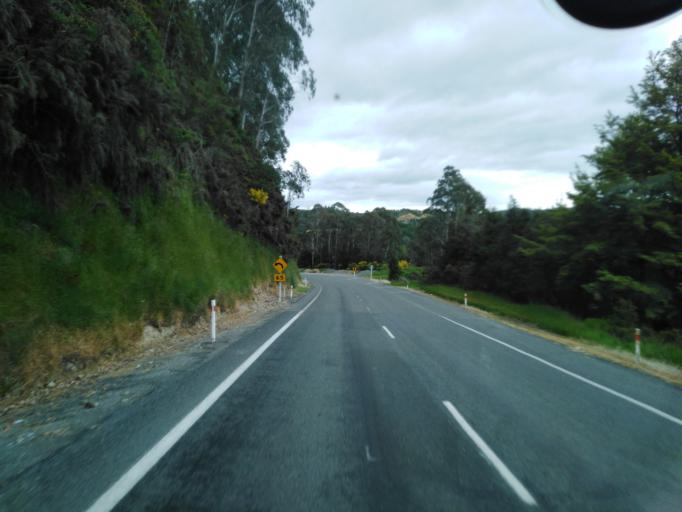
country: NZ
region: Tasman
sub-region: Tasman District
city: Wakefield
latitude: -41.6298
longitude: 172.7015
